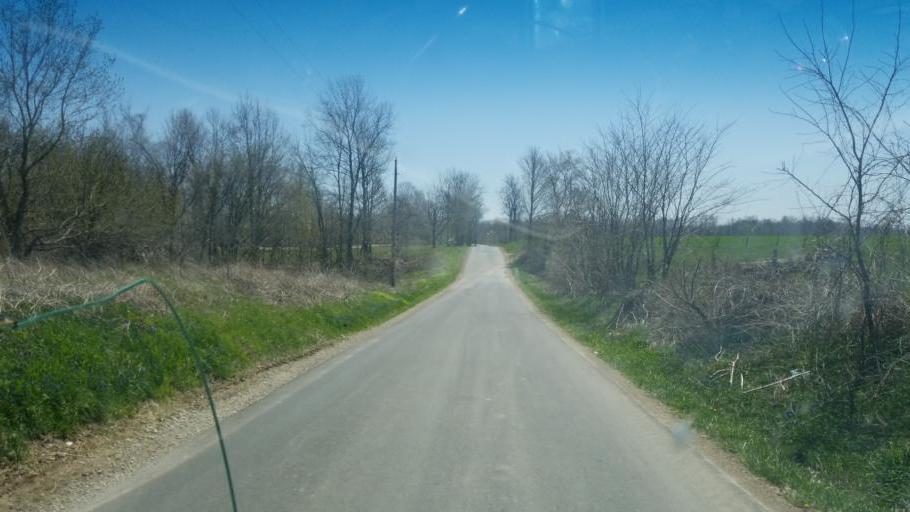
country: US
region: Ohio
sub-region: Huron County
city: Greenwich
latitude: 41.0621
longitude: -82.5121
